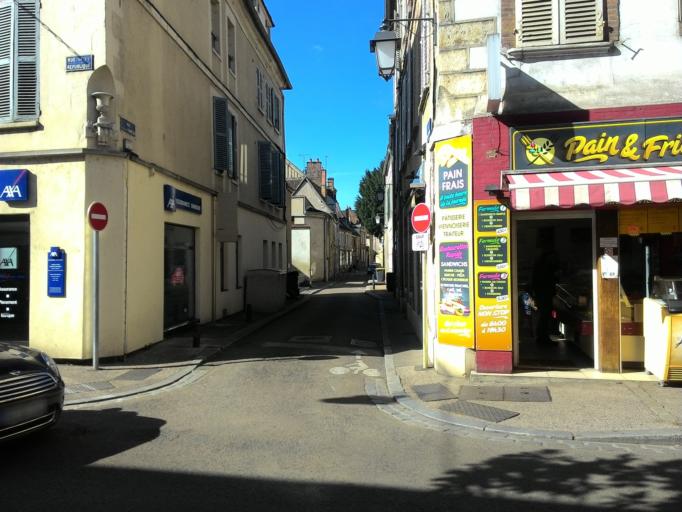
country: FR
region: Bourgogne
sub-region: Departement de l'Yonne
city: Sens
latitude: 48.1965
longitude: 3.2831
